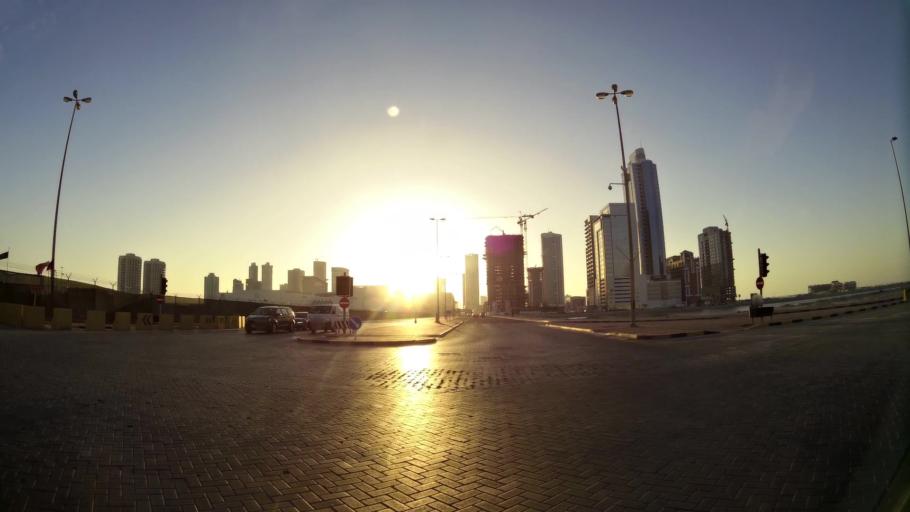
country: BH
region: Manama
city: Jidd Hafs
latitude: 26.2351
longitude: 50.5605
